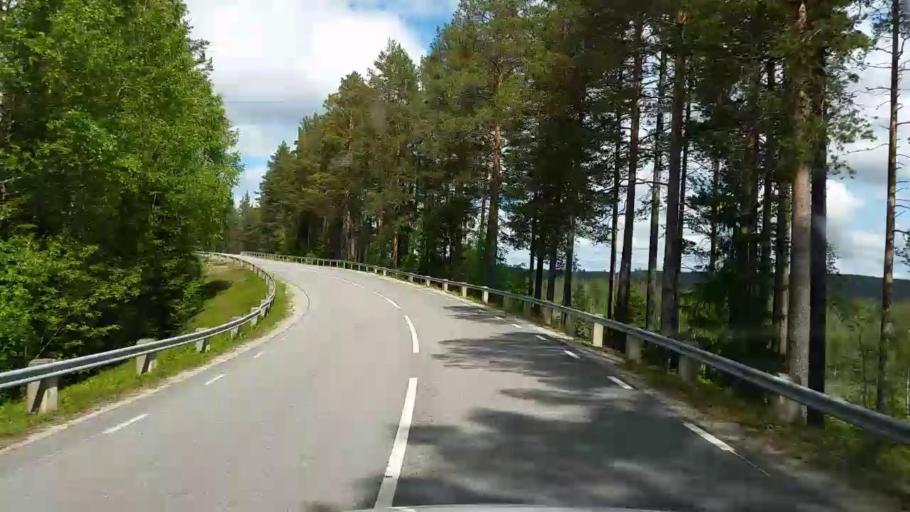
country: SE
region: Gaevleborg
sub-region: Bollnas Kommun
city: Vittsjo
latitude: 61.1245
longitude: 16.1759
